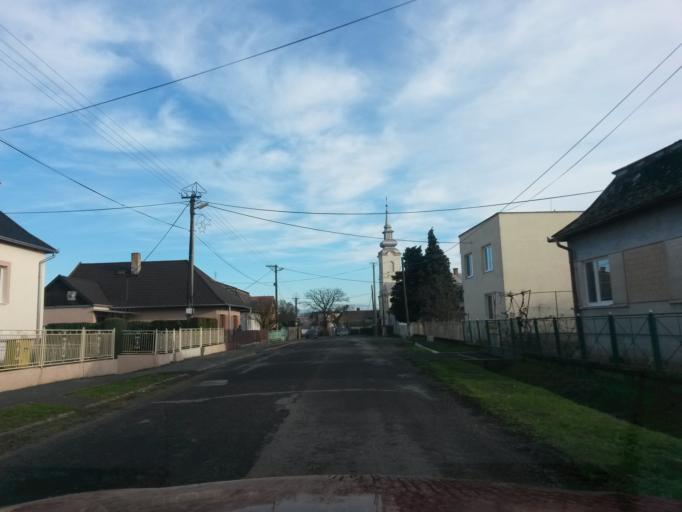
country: SK
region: Kosicky
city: Cierna nad Tisou
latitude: 48.5396
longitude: 22.0233
